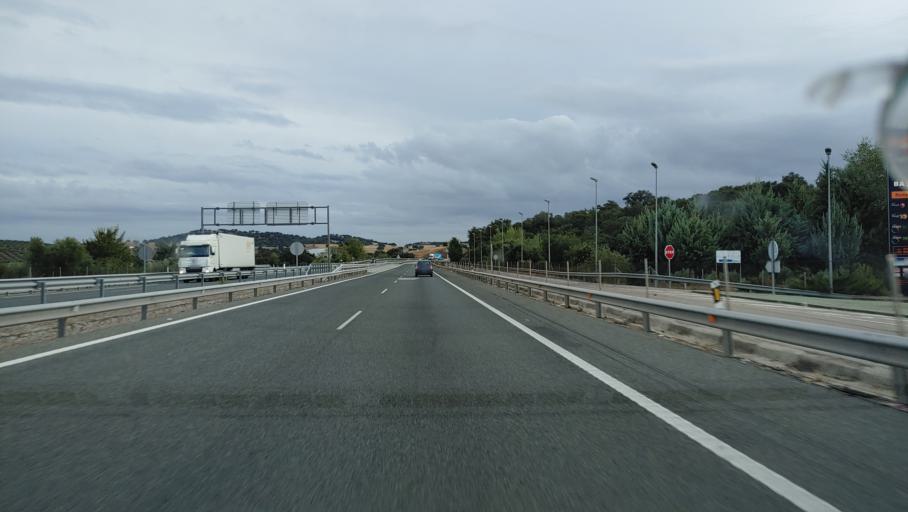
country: ES
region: Andalusia
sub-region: Provincia de Jaen
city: Santa Elena
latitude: 38.3368
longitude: -3.5443
